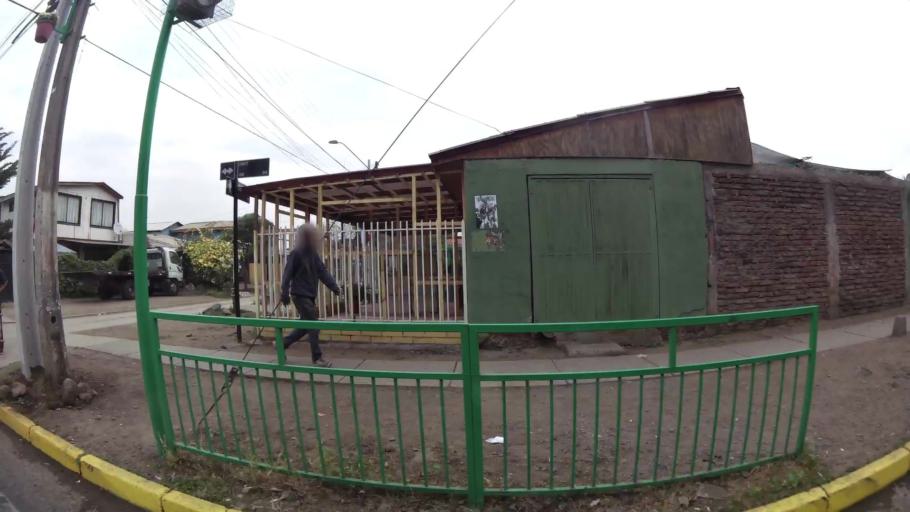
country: CL
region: Santiago Metropolitan
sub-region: Provincia de Chacabuco
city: Chicureo Abajo
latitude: -33.1953
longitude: -70.6753
